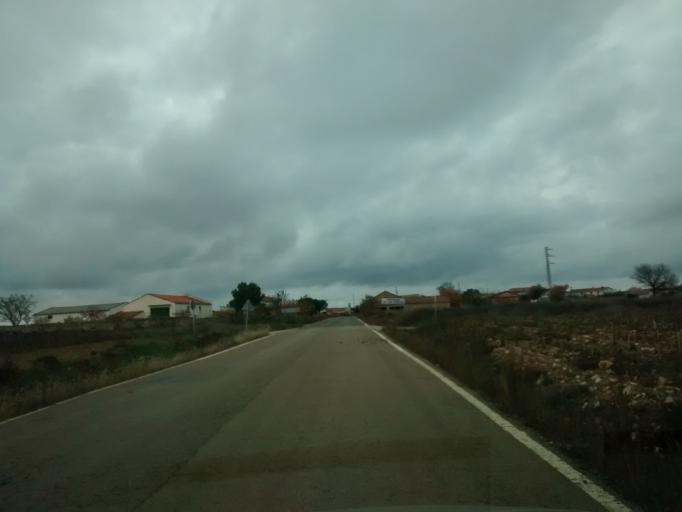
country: ES
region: Aragon
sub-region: Provincia de Zaragoza
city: Torralba de los Frailes
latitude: 41.0373
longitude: -1.6552
